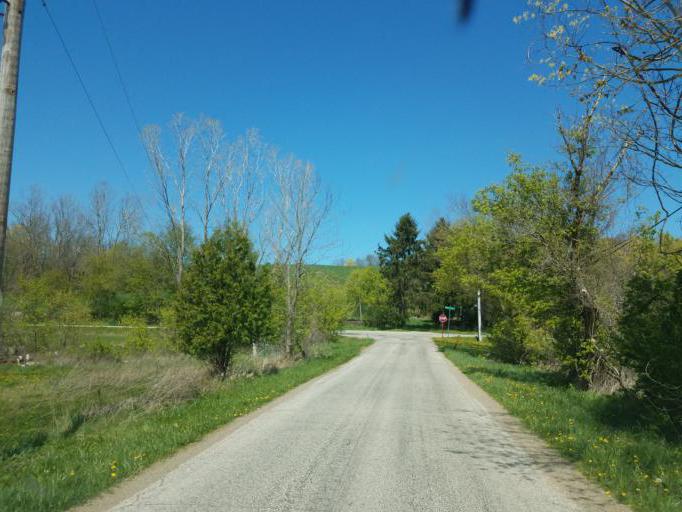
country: US
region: Ohio
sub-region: Richland County
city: Lincoln Heights
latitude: 40.7337
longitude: -82.3996
